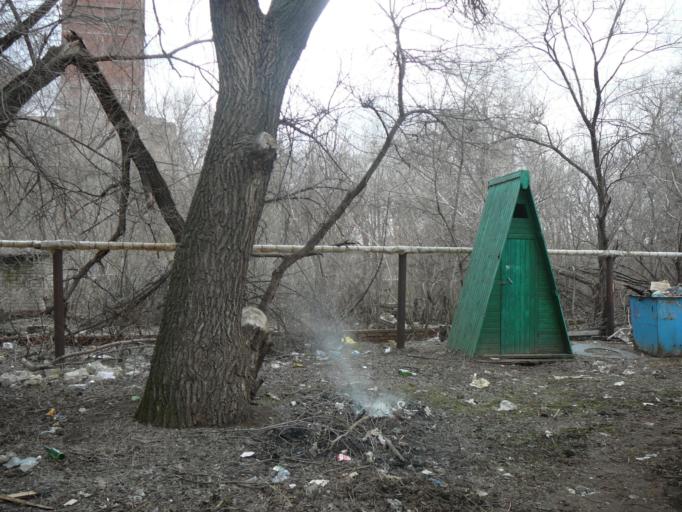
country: RU
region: Saratov
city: Privolzhskiy
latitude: 51.4127
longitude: 46.0513
